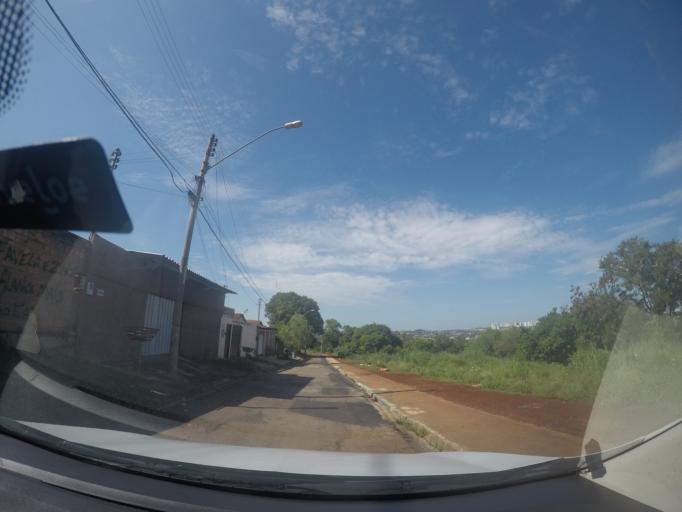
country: BR
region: Goias
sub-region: Goiania
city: Goiania
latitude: -16.6635
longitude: -49.1935
